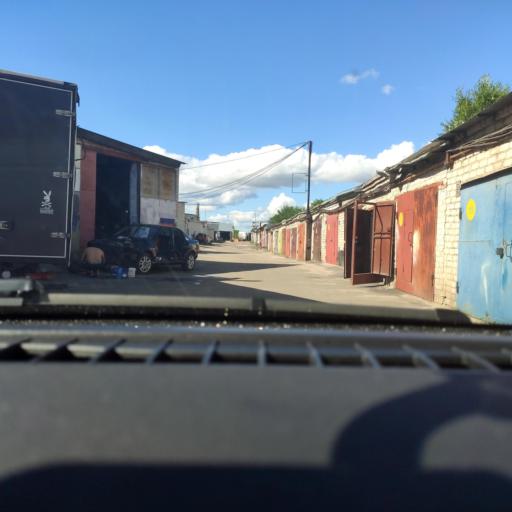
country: RU
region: Voronezj
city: Somovo
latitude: 51.6648
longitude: 39.2917
